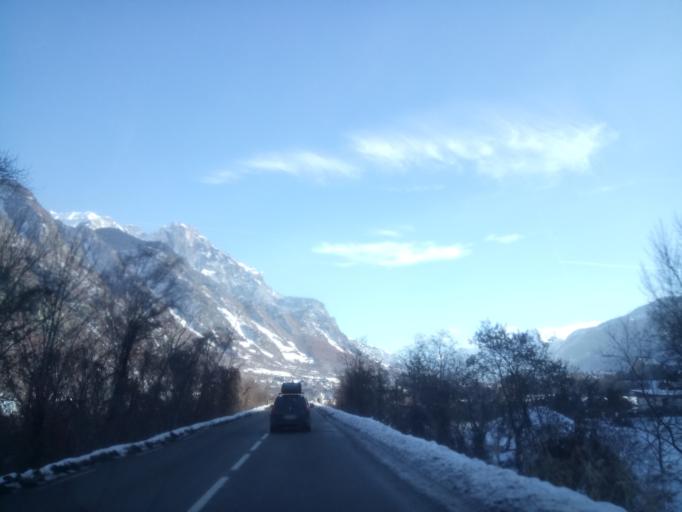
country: FR
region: Rhone-Alpes
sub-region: Departement de la Savoie
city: Villargondran
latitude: 45.2669
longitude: 6.3735
